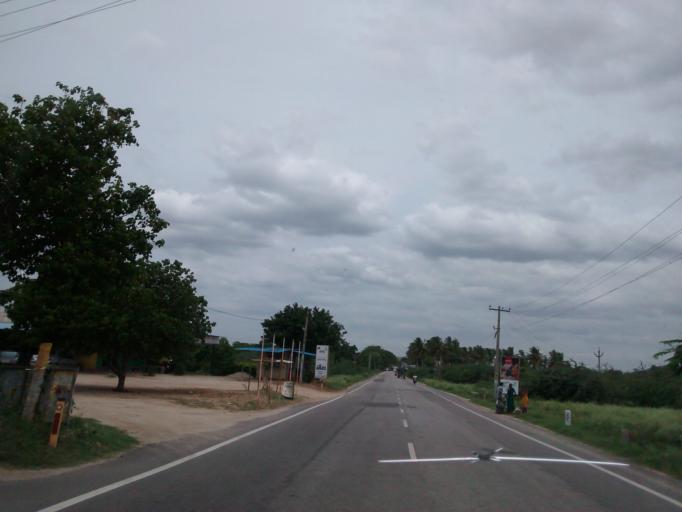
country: IN
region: Andhra Pradesh
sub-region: Chittoor
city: Chittoor
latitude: 13.2812
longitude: 79.0411
